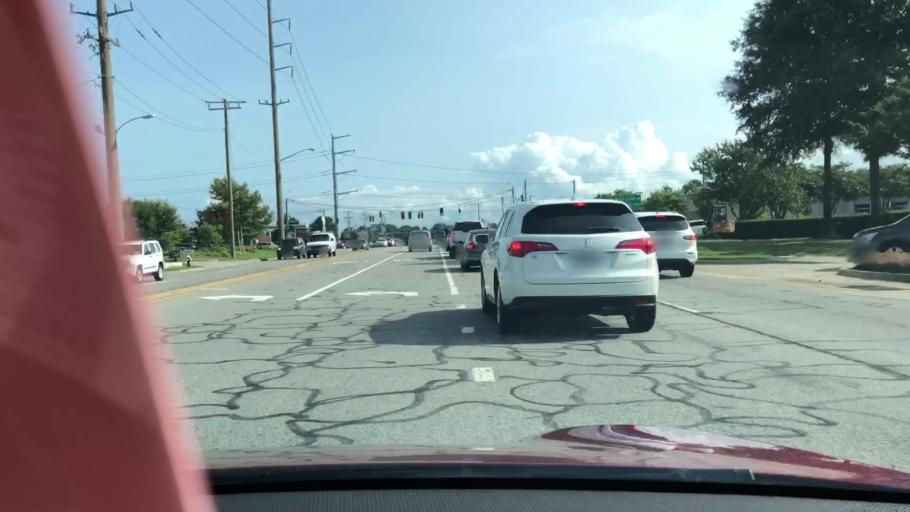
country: US
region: Virginia
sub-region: City of Virginia Beach
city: Virginia Beach
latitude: 36.8521
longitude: -76.0226
